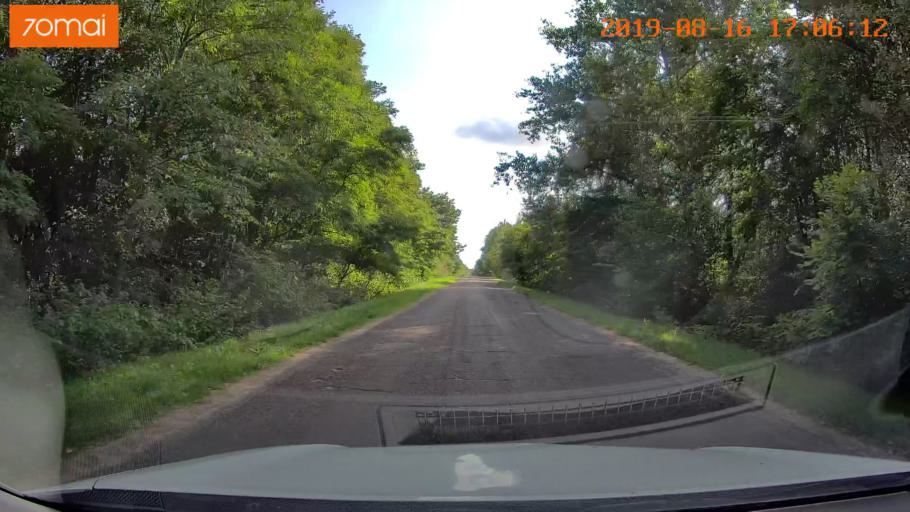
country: BY
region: Mogilev
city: Hlusha
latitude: 53.2294
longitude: 28.9357
